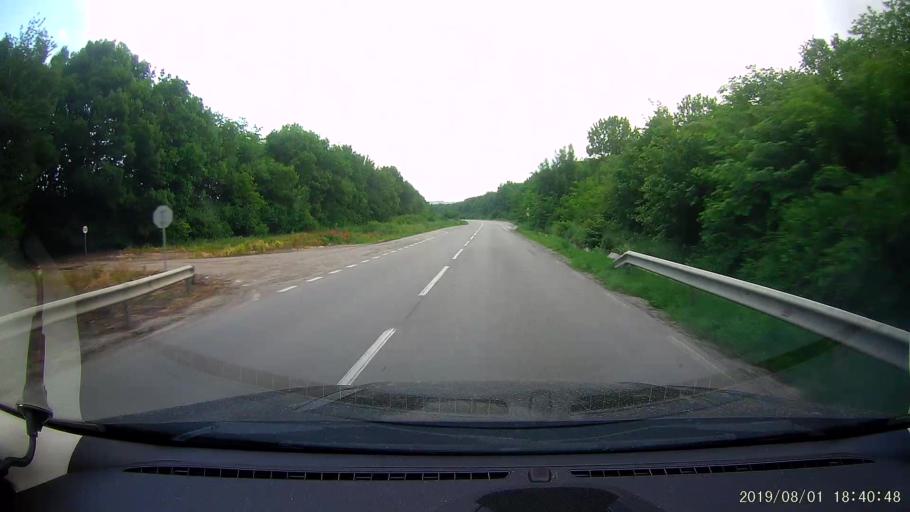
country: BG
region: Shumen
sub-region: Obshtina Khitrino
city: Gara Khitrino
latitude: 43.3585
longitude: 26.9209
